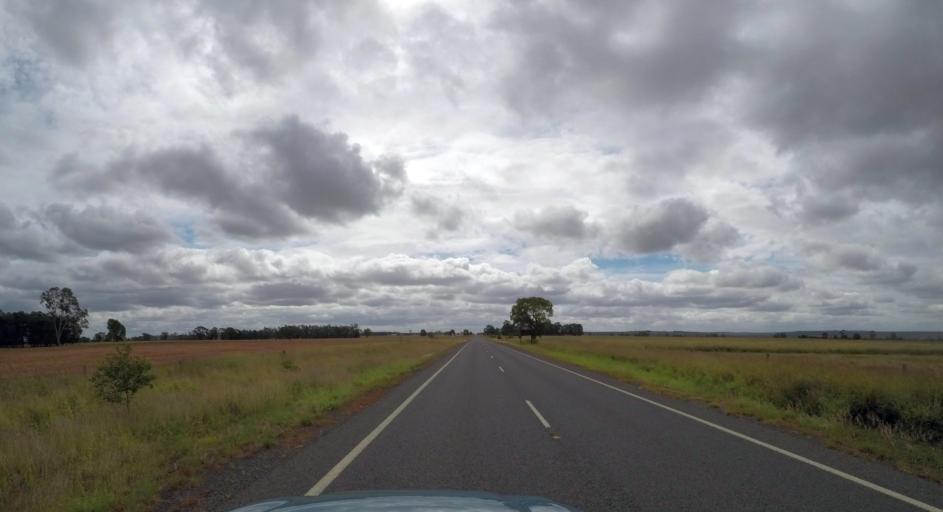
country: AU
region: Queensland
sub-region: South Burnett
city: Kingaroy
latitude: -26.3887
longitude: 151.2447
